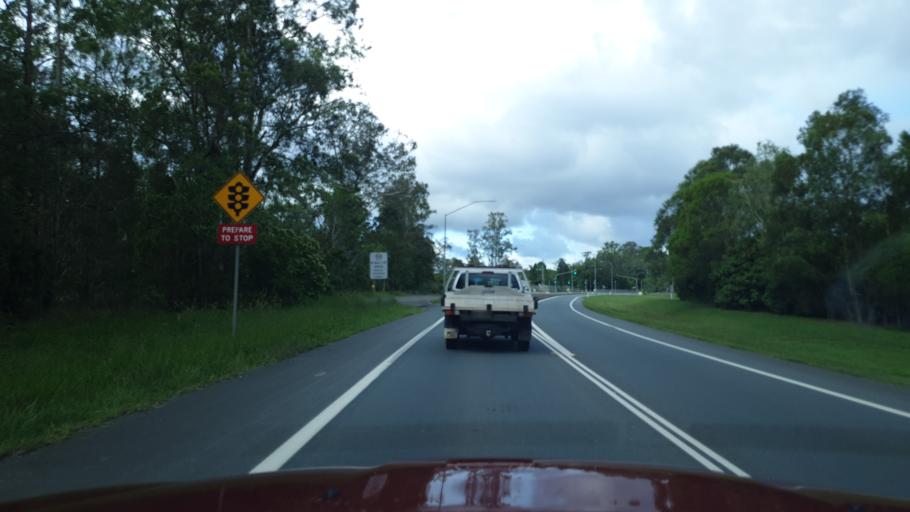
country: AU
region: Queensland
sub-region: Sunshine Coast
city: Little Mountain
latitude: -26.8137
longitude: 152.9645
